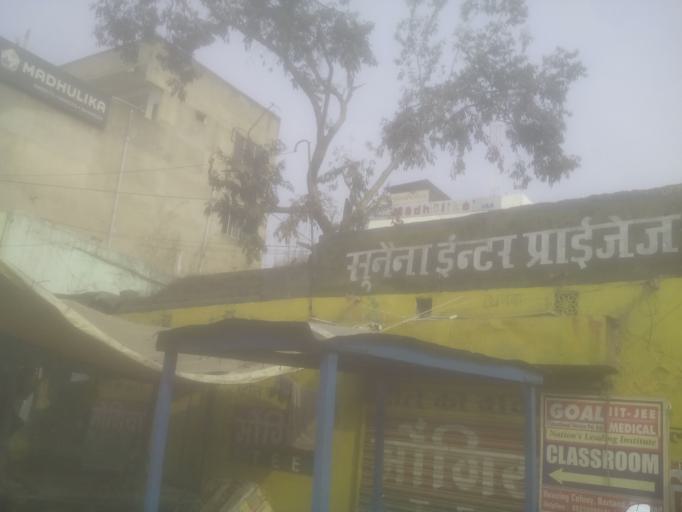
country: IN
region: Jharkhand
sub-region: Dhanbad
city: Dhanbad
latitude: 23.8068
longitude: 86.4319
